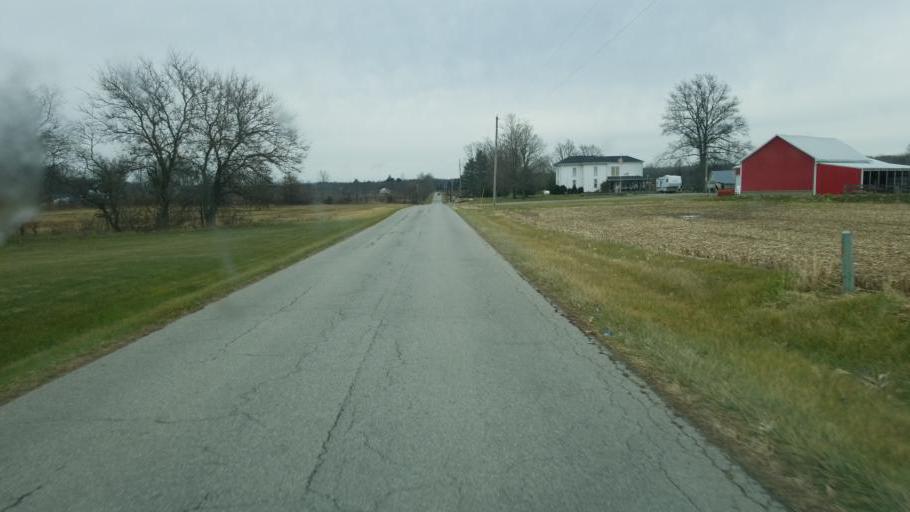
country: US
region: Ohio
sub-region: Delaware County
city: Ashley
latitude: 40.3817
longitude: -82.8861
